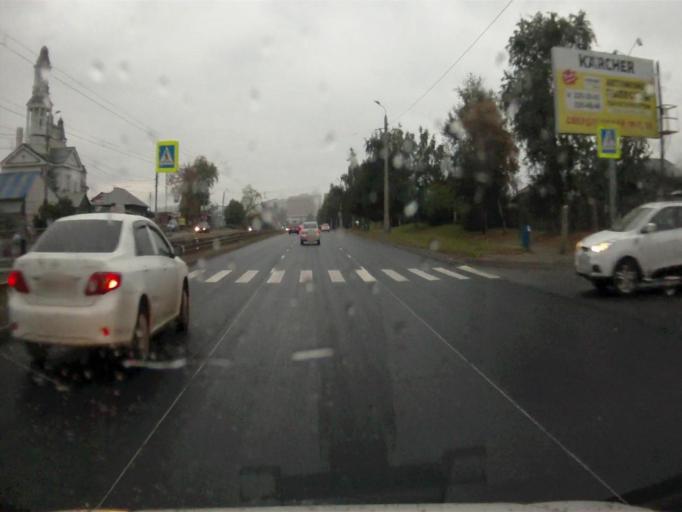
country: RU
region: Chelyabinsk
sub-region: Gorod Chelyabinsk
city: Chelyabinsk
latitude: 55.1852
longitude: 61.3680
